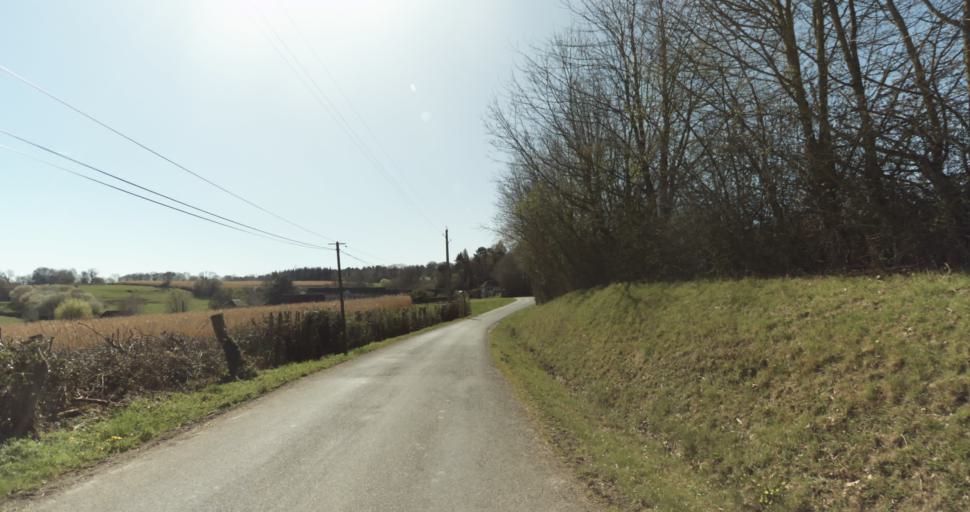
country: FR
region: Lower Normandy
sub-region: Departement du Calvados
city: Saint-Pierre-sur-Dives
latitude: 49.0146
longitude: 0.0577
